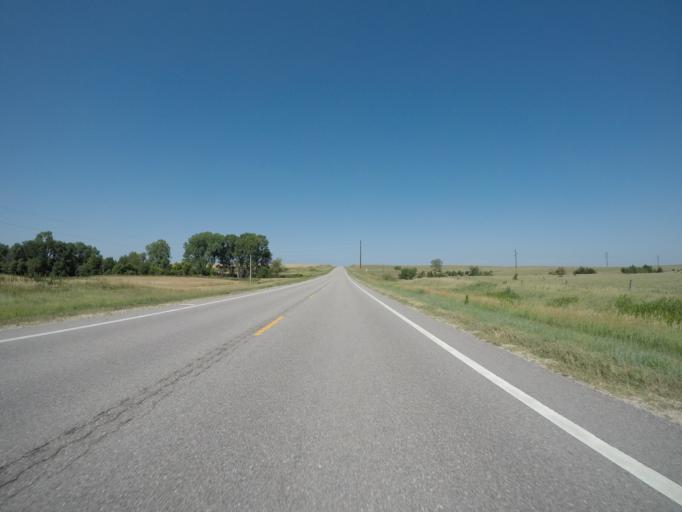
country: US
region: Kansas
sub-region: Cloud County
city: Concordia
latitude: 39.3647
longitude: -97.5563
